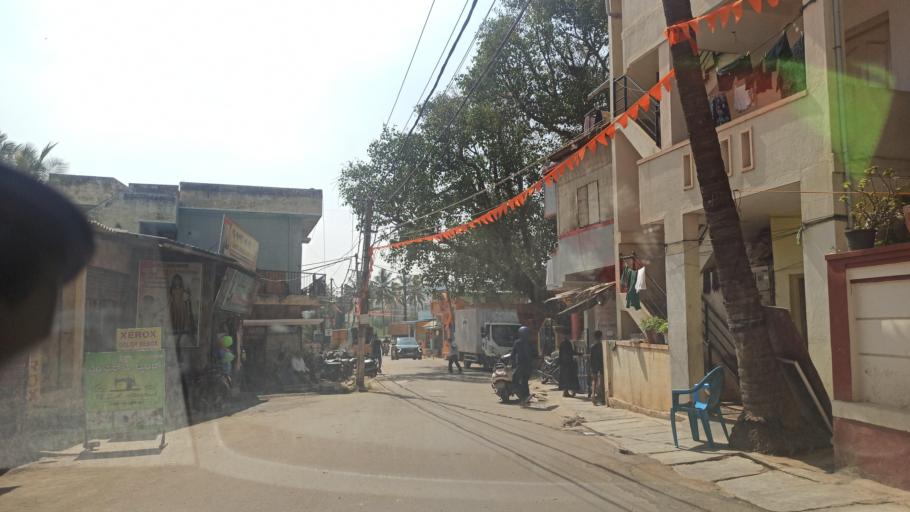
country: IN
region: Karnataka
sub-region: Bangalore Urban
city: Yelahanka
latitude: 13.0643
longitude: 77.6009
